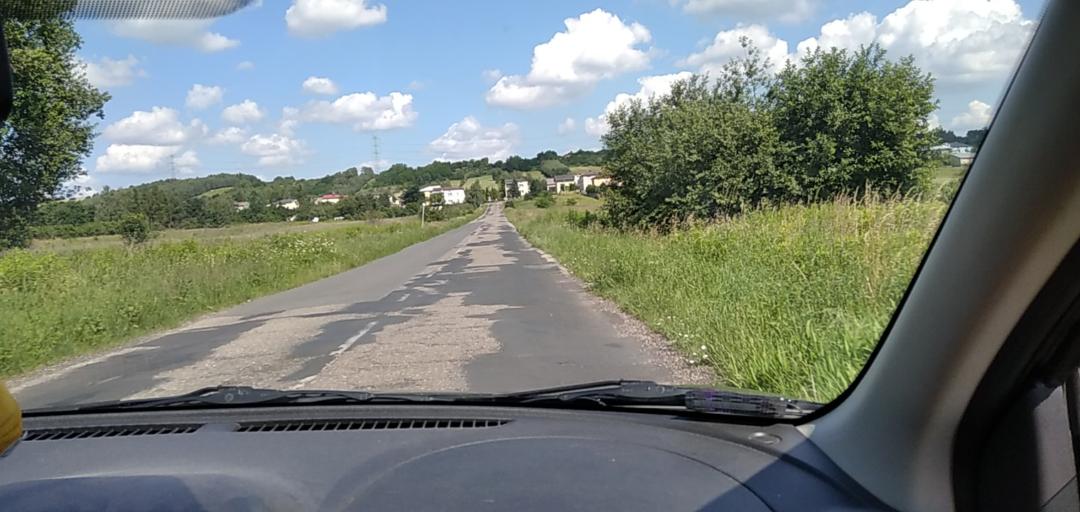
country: PL
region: Silesian Voivodeship
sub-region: Powiat bedzinski
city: Psary
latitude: 50.4003
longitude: 19.1363
